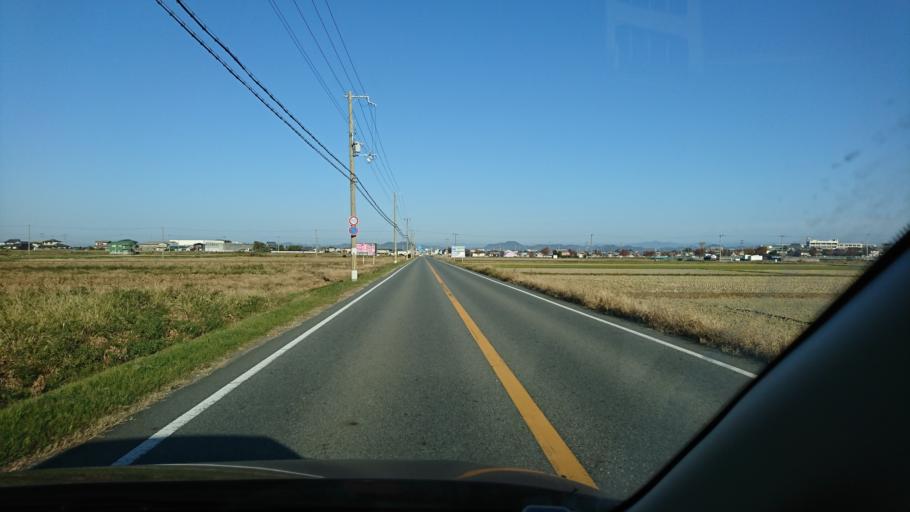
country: JP
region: Hyogo
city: Kakogawacho-honmachi
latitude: 34.7409
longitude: 134.9023
